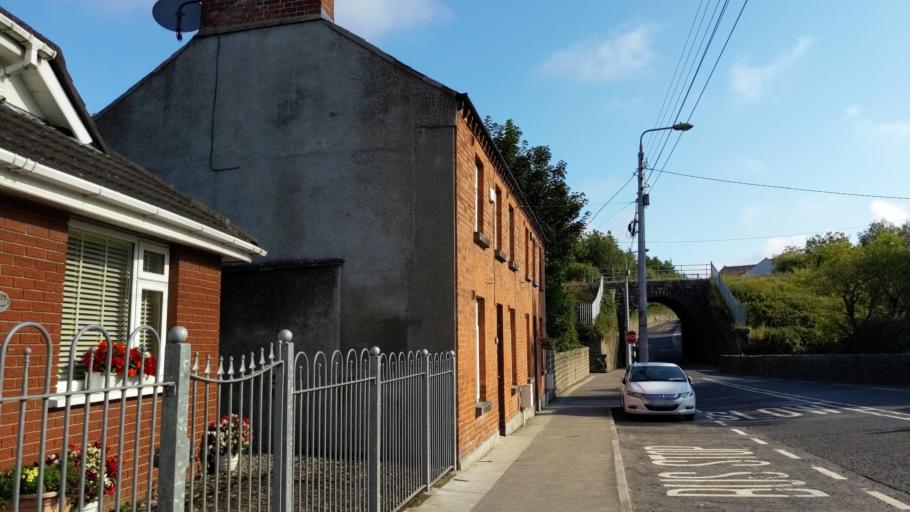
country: IE
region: Leinster
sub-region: Lu
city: Drogheda
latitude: 53.7075
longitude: -6.3486
